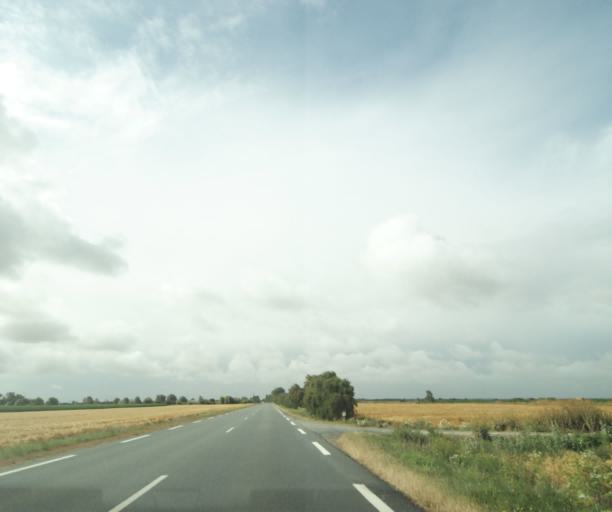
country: FR
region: Poitou-Charentes
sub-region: Departement de la Charente-Maritime
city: Andilly
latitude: 46.2663
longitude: -1.0674
